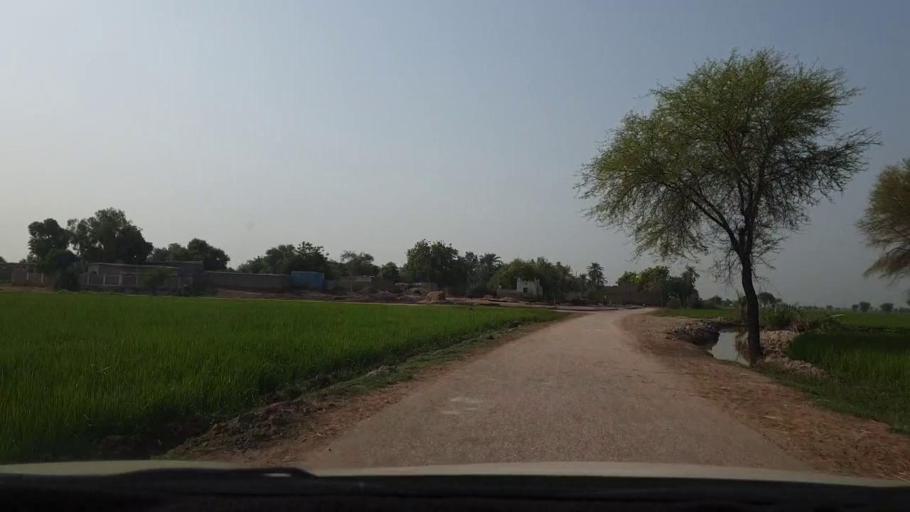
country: PK
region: Sindh
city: Goth Garelo
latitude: 27.4642
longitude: 68.0909
